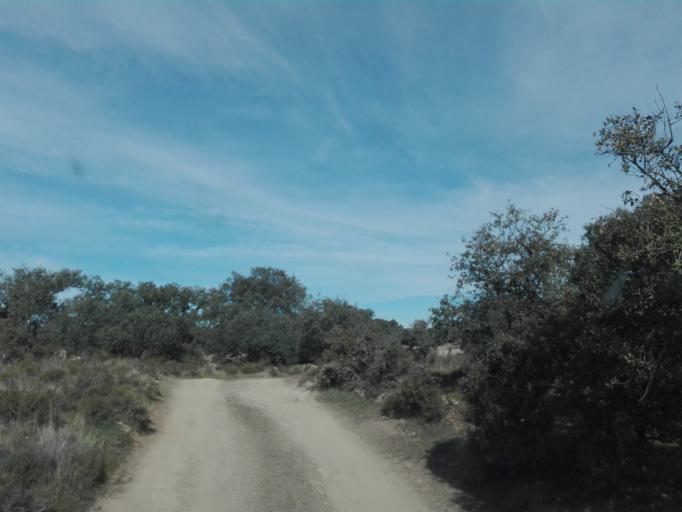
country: ES
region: Extremadura
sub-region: Provincia de Badajoz
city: Azuaga
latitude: 38.2306
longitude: -5.7411
